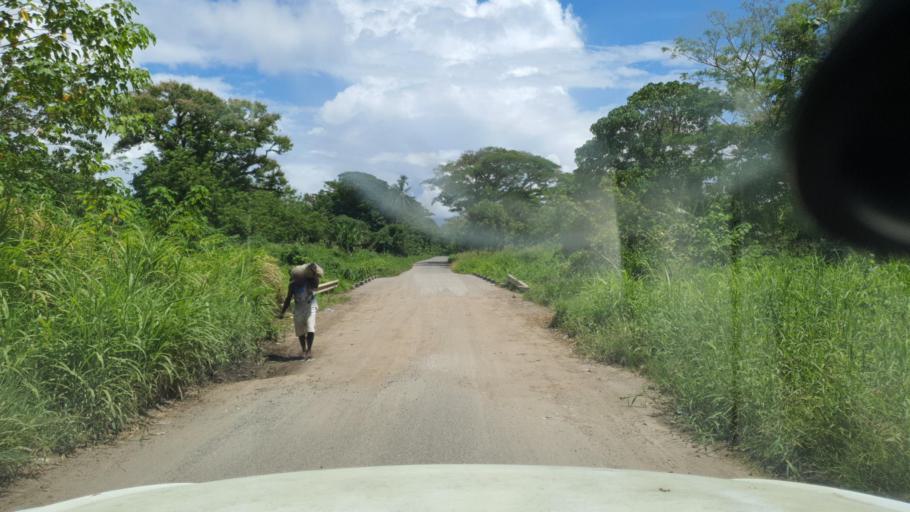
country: SB
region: Guadalcanal
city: Honiara
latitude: -9.3188
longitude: 159.7984
